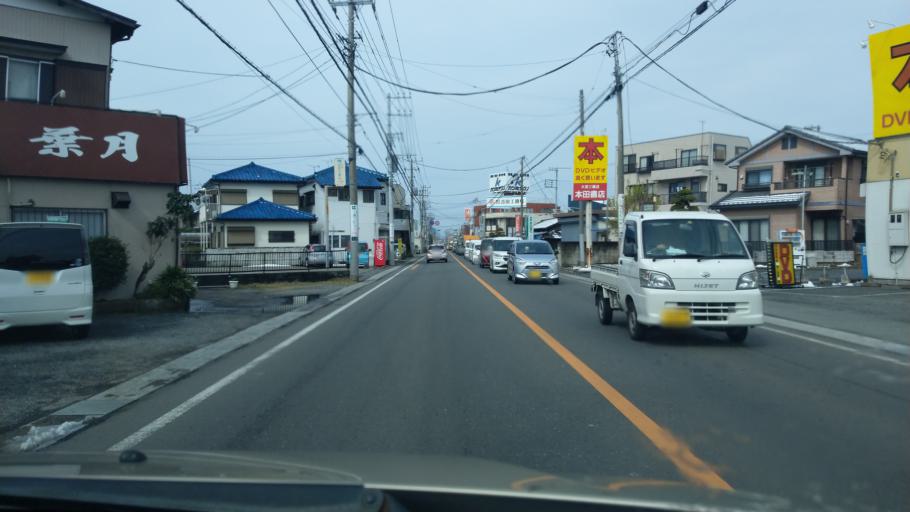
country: JP
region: Saitama
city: Yono
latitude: 35.9108
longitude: 139.5901
